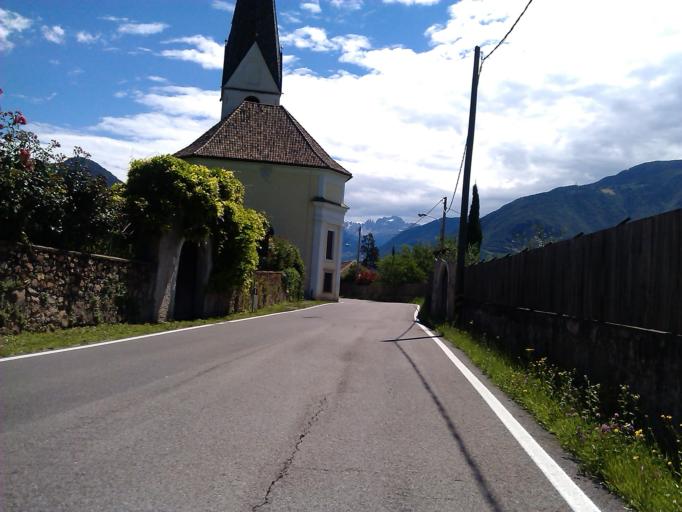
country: IT
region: Trentino-Alto Adige
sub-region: Bolzano
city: Bolzano
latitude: 46.5009
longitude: 11.3068
